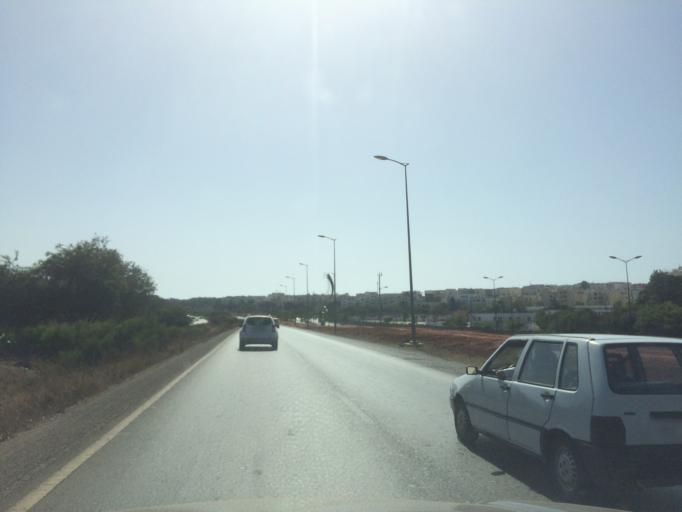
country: MA
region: Rabat-Sale-Zemmour-Zaer
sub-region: Skhirate-Temara
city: Temara
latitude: 33.9653
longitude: -6.8957
